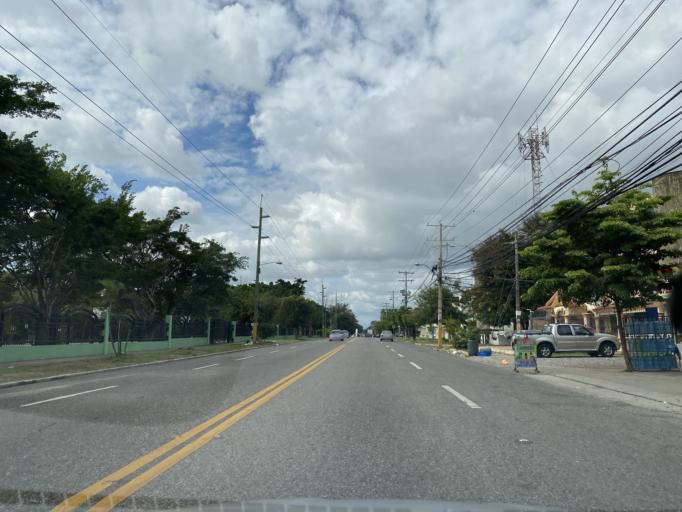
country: DO
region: Santo Domingo
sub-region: Santo Domingo
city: Santo Domingo Este
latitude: 18.4813
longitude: -69.8526
